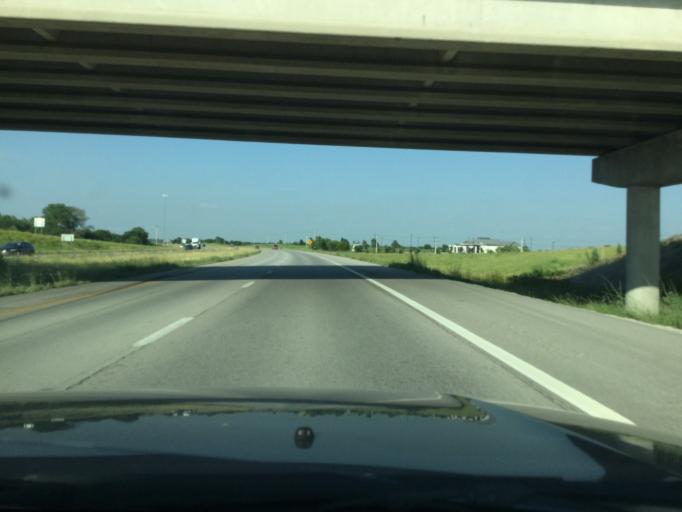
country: US
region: Kansas
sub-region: Douglas County
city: Eudora
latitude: 38.9294
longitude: -95.0949
